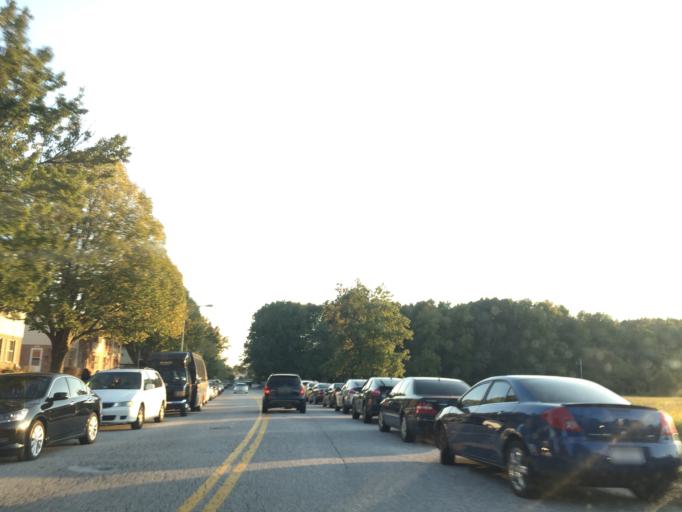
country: US
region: Maryland
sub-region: Baltimore County
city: Essex
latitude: 39.2947
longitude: -76.4472
